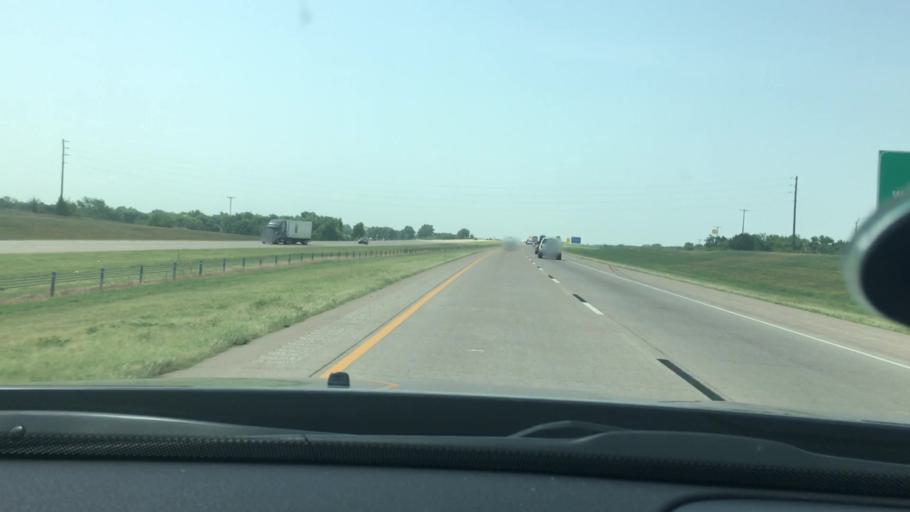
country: US
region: Oklahoma
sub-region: Garvin County
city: Wynnewood
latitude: 34.6582
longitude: -97.2213
